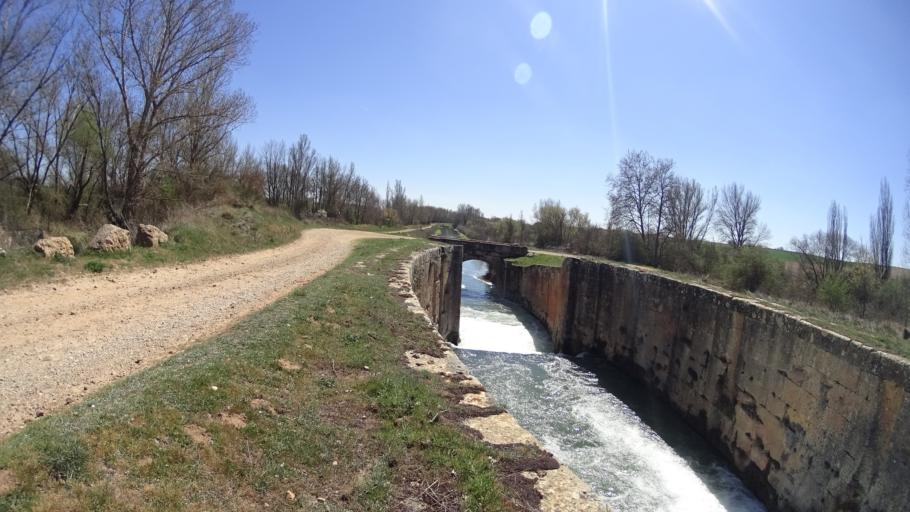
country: ES
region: Castille and Leon
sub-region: Provincia de Burgos
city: Rezmondo
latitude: 42.4825
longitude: -4.2609
